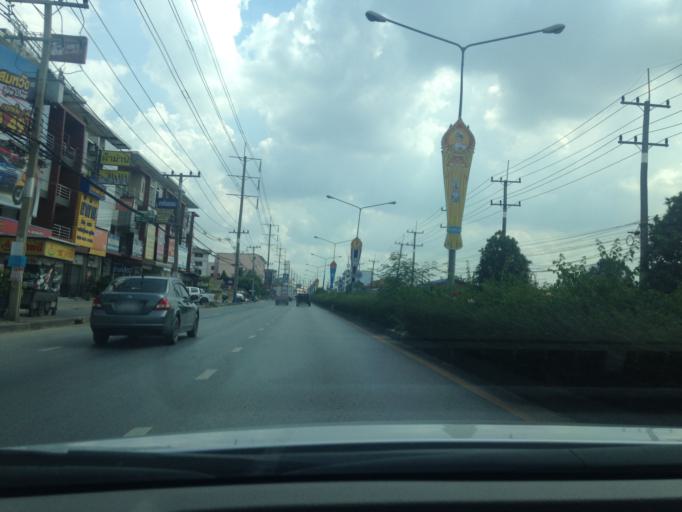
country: TH
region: Pathum Thani
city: Sam Khok
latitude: 14.0502
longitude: 100.5248
